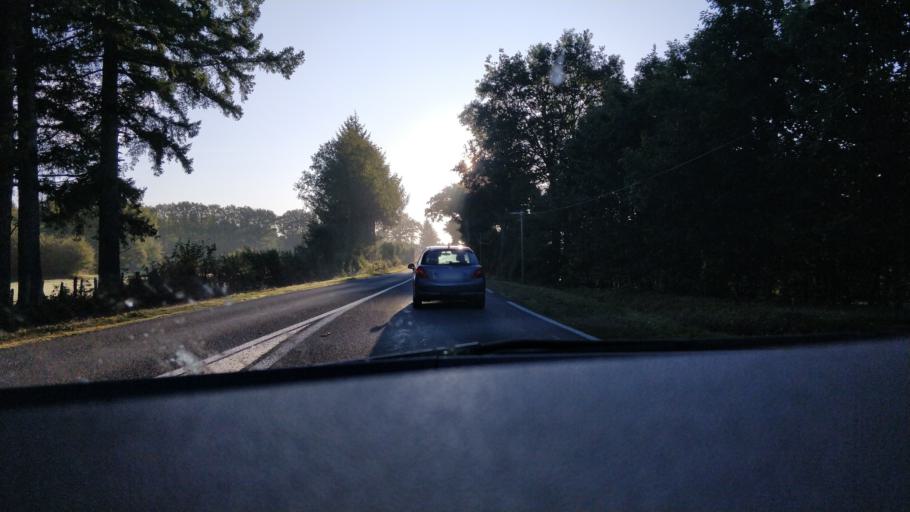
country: FR
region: Limousin
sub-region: Departement de la Creuse
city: Bourganeuf
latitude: 45.9473
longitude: 1.7008
